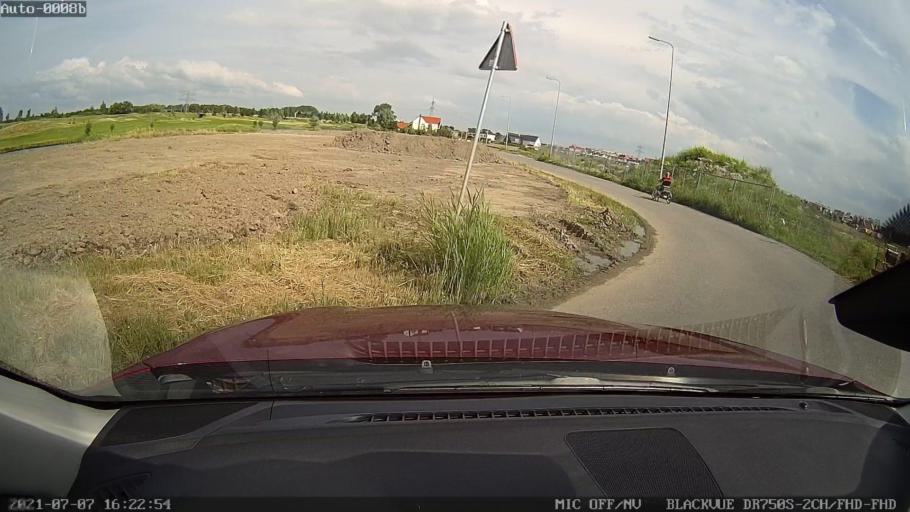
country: NL
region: Zeeland
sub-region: Gemeente Middelburg
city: Middelburg
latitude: 51.4873
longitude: 3.6404
